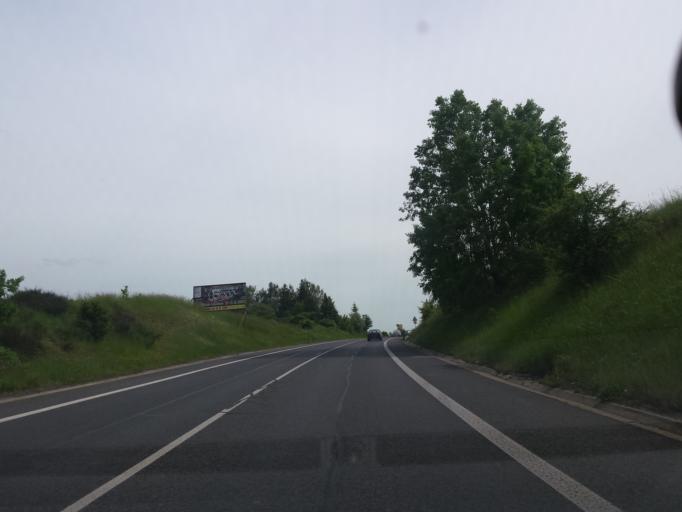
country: CZ
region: Liberecky
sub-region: Okres Ceska Lipa
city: Ceska Lipa
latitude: 50.6474
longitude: 14.5361
